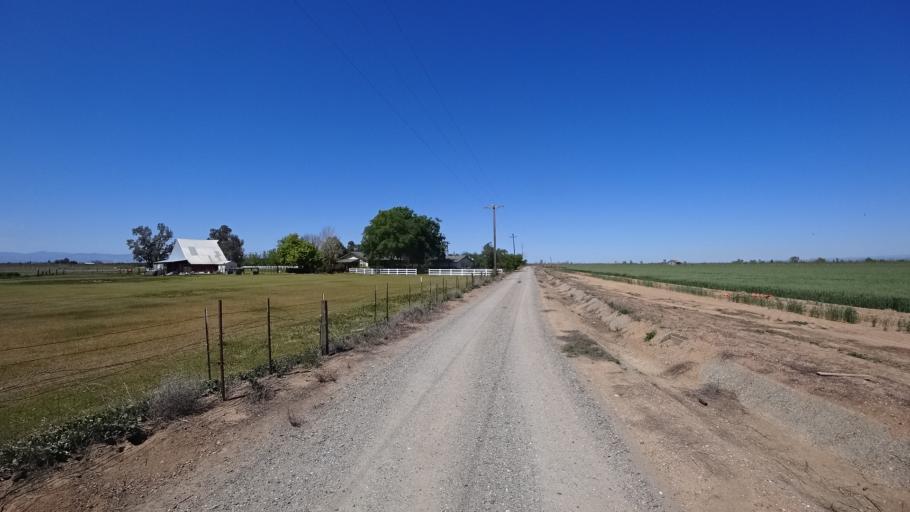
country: US
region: California
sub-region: Glenn County
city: Hamilton City
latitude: 39.7315
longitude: -122.0901
